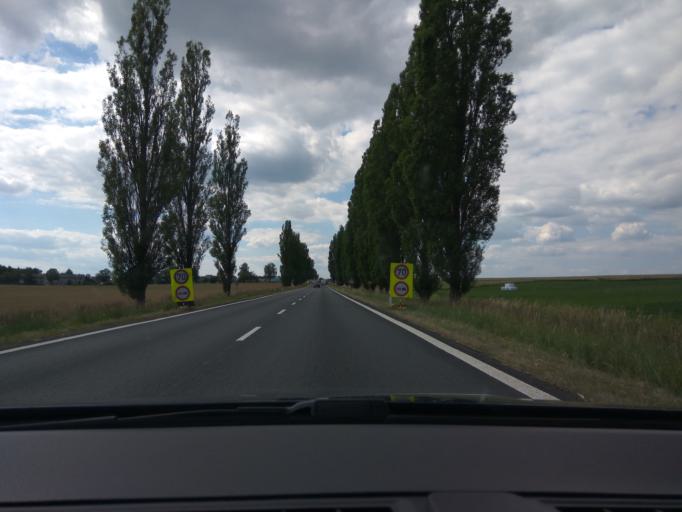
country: CZ
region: Jihocesky
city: Kovarov
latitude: 49.4989
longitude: 14.2236
